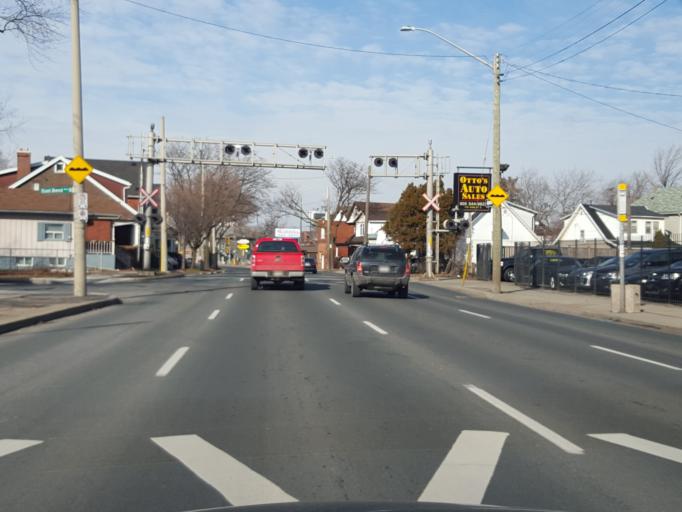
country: CA
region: Ontario
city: Hamilton
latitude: 43.2464
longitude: -79.8269
